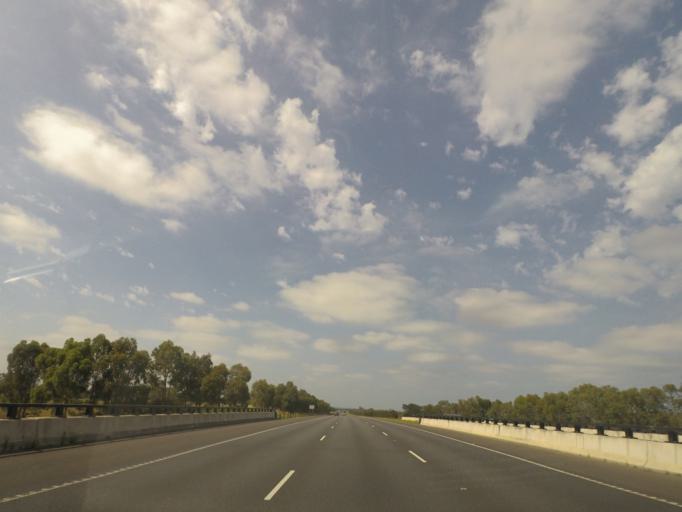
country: AU
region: Victoria
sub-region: Frankston
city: Sandhurst
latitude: -38.0412
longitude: 145.1876
